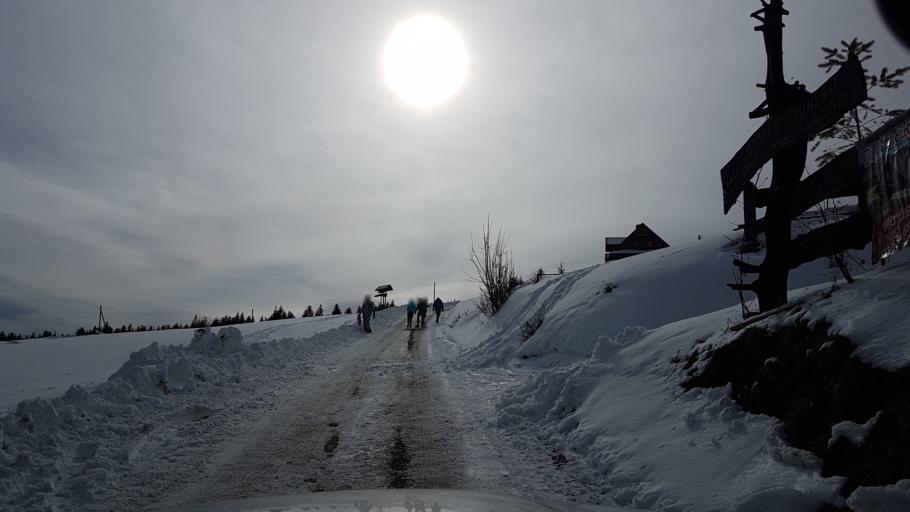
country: PL
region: Lesser Poland Voivodeship
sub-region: Powiat nowosadecki
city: Rytro
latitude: 49.4199
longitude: 20.6234
